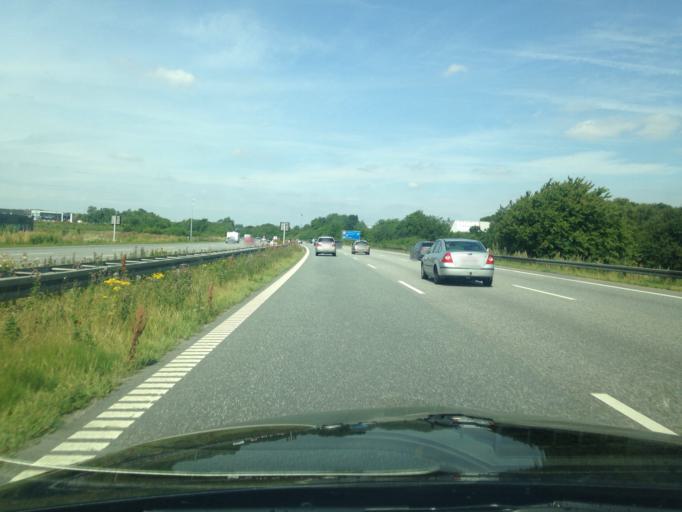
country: DK
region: South Denmark
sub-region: Fredericia Kommune
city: Snoghoj
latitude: 55.5283
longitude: 9.7244
